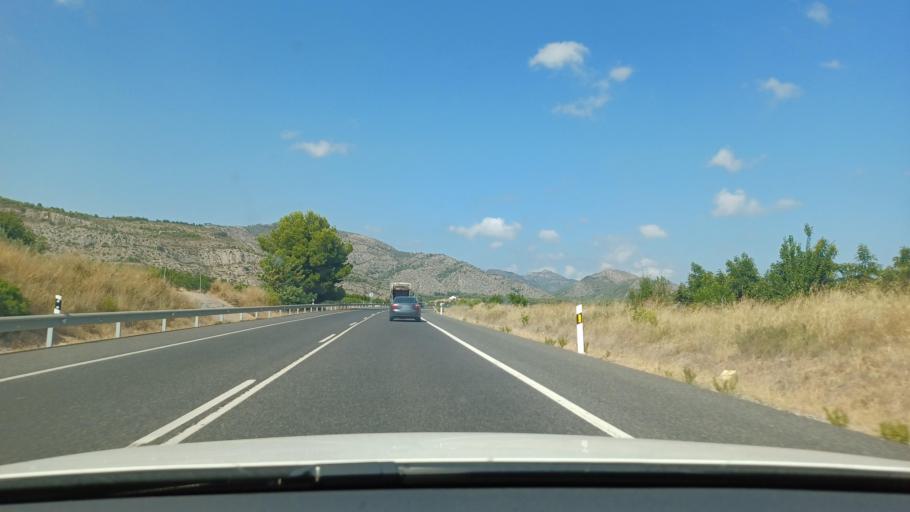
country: ES
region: Valencia
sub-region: Provincia de Castello
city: Borriol
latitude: 40.0260
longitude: -0.0346
